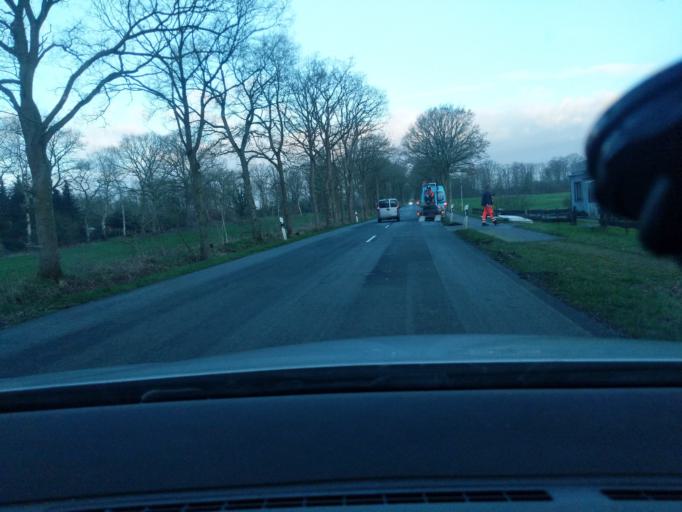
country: DE
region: Lower Saxony
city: Flogeln
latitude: 53.6323
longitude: 8.7949
